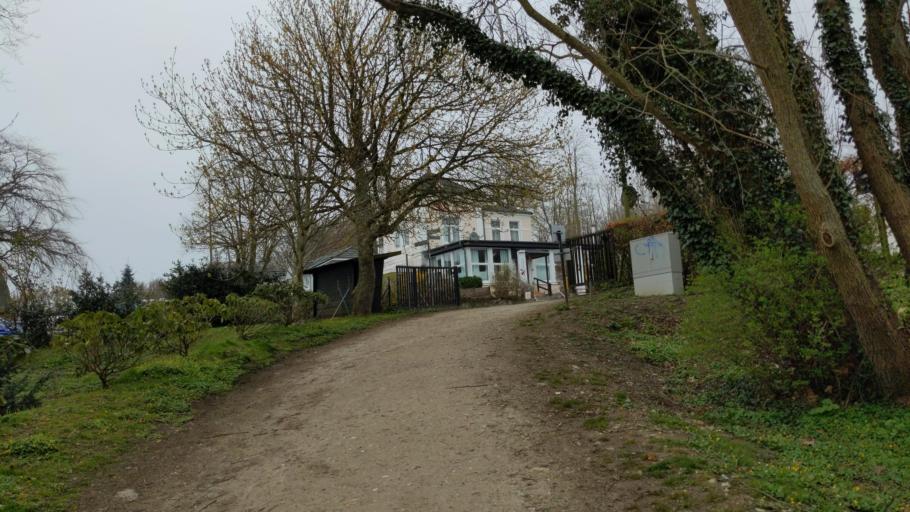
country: DE
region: Schleswig-Holstein
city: Glucksburg
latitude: 54.8351
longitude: 9.5460
